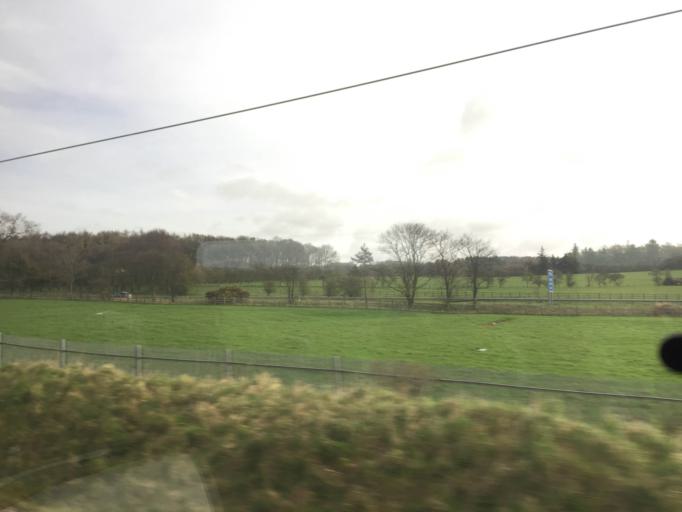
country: GB
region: England
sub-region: Lancashire
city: Garstang
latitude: 53.9133
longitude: -2.7561
